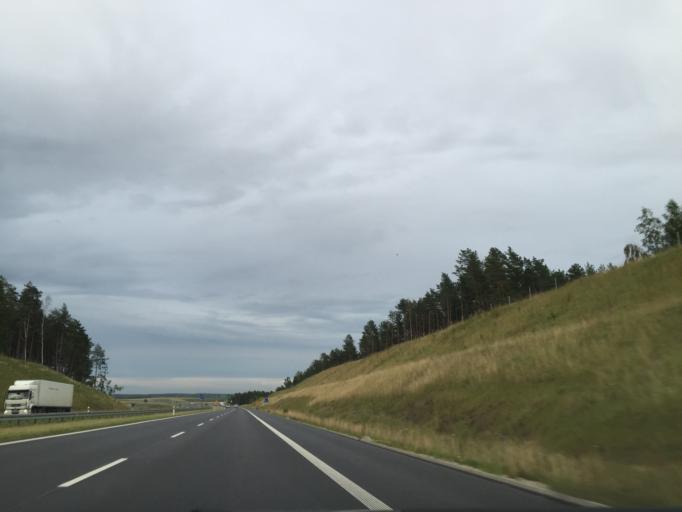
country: PL
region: Podlasie
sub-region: Powiat zambrowski
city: Rutki-Kossaki
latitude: 53.0840
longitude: 22.4644
